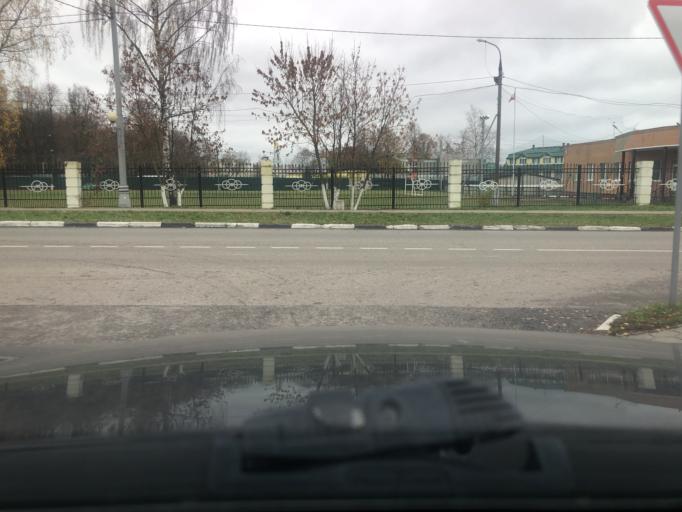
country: RU
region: Moskovskaya
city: Sergiyev Posad
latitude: 56.3187
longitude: 38.1346
